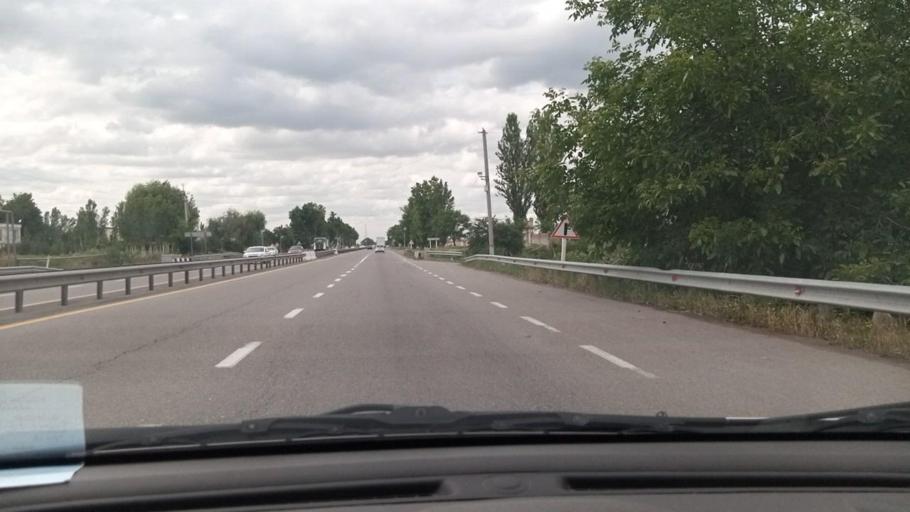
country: UZ
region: Toshkent Shahri
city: Bektemir
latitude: 41.1518
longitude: 69.4267
